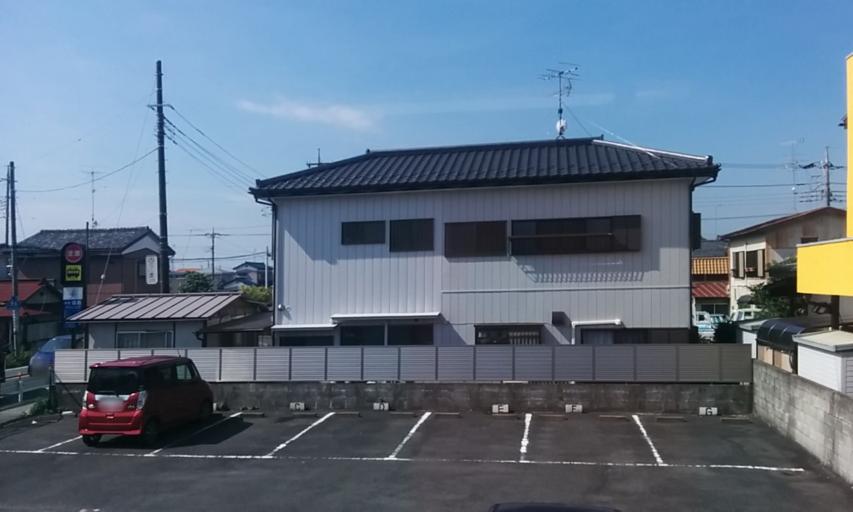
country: JP
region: Saitama
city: Kazo
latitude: 36.1219
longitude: 139.5983
